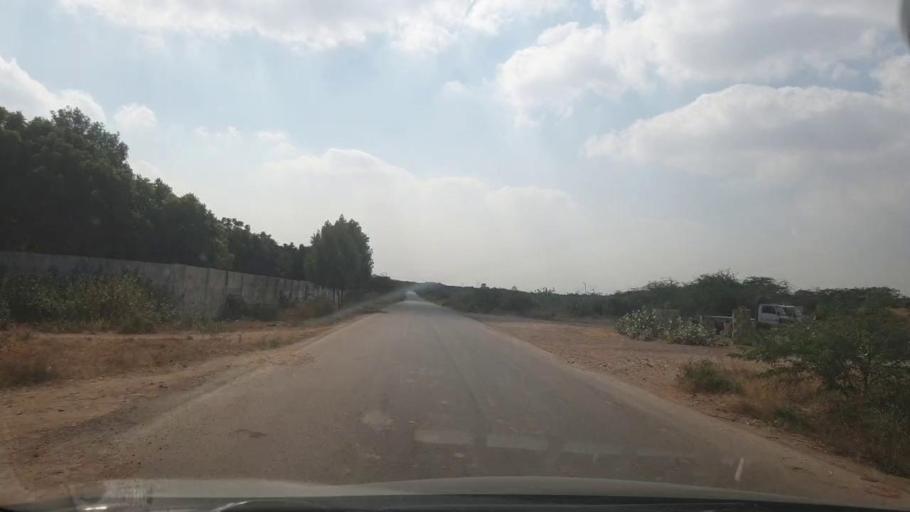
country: PK
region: Sindh
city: Malir Cantonment
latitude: 25.0202
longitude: 67.3545
